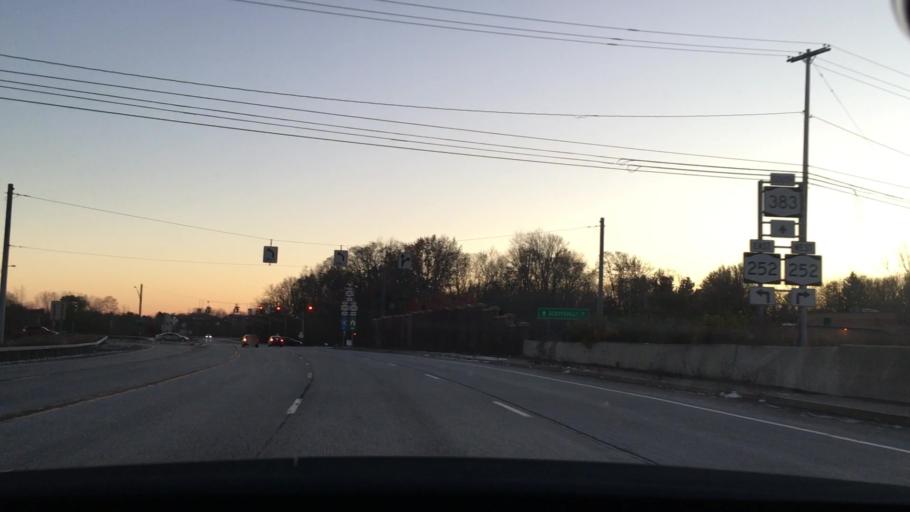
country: US
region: New York
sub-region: Monroe County
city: North Gates
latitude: 43.0941
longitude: -77.6809
